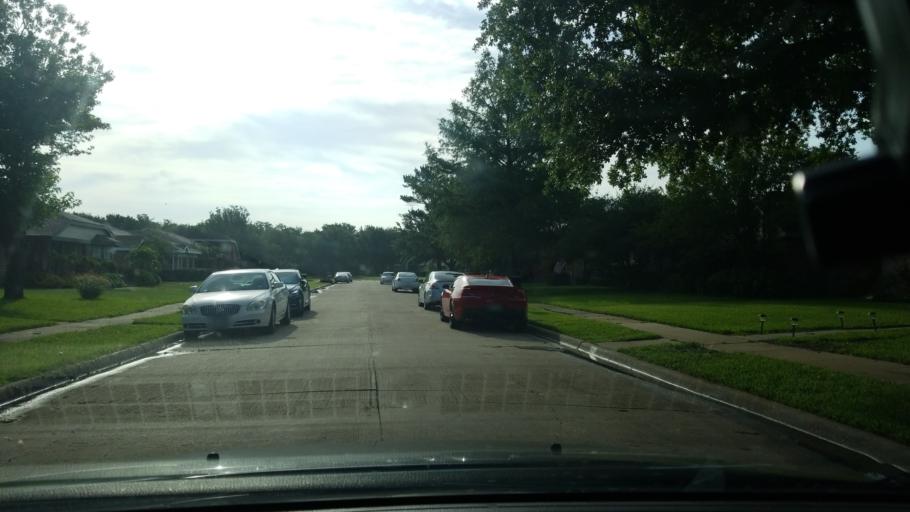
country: US
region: Texas
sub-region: Dallas County
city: Mesquite
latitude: 32.8018
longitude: -96.6023
